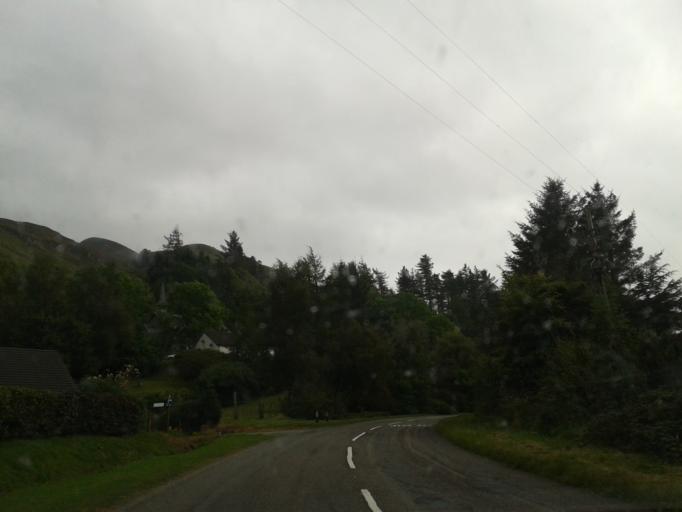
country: GB
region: Scotland
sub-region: Highland
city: Fort William
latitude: 57.2787
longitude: -5.5140
